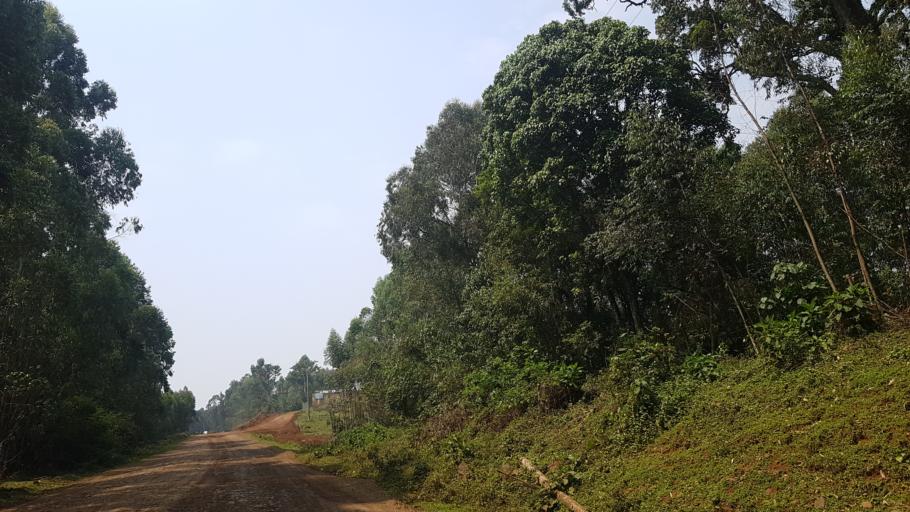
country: ET
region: Oromiya
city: Gore
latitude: 7.7934
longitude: 35.4568
